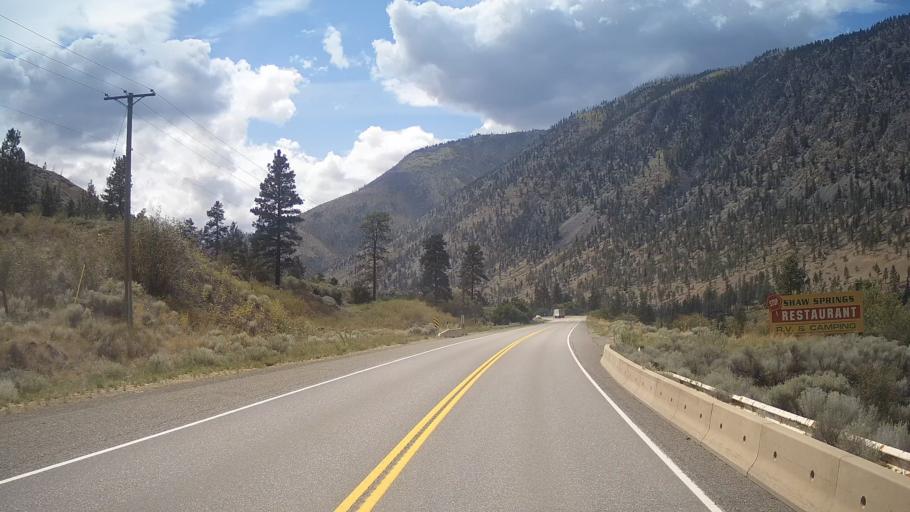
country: CA
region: British Columbia
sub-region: Thompson-Nicola Regional District
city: Ashcroft
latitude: 50.3436
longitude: -121.3916
